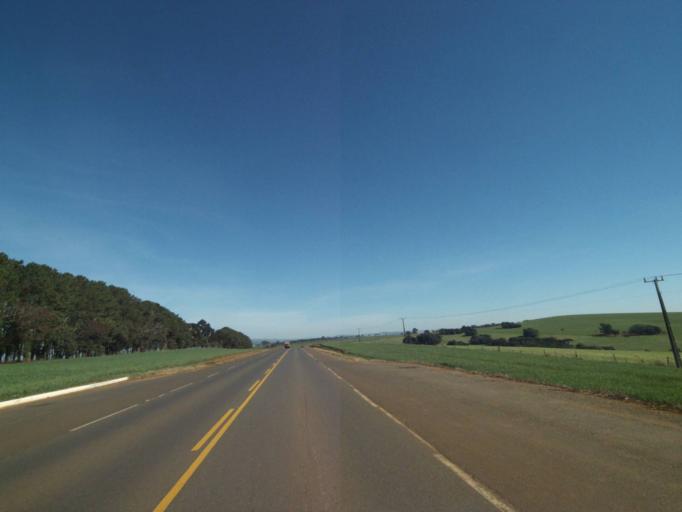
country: BR
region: Parana
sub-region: Tibagi
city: Tibagi
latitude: -24.4183
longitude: -50.3694
